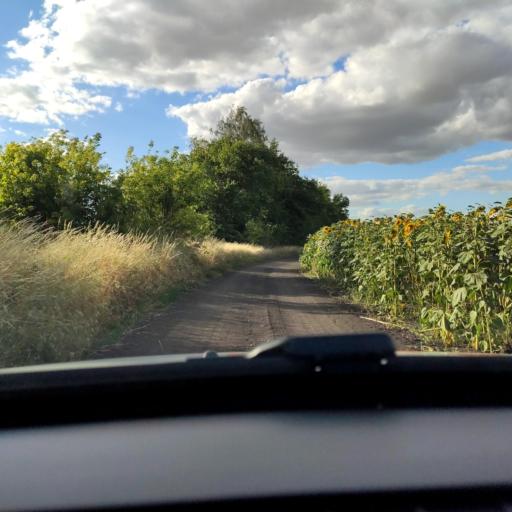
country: RU
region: Voronezj
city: Verkhnyaya Khava
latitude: 51.5946
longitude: 39.8420
